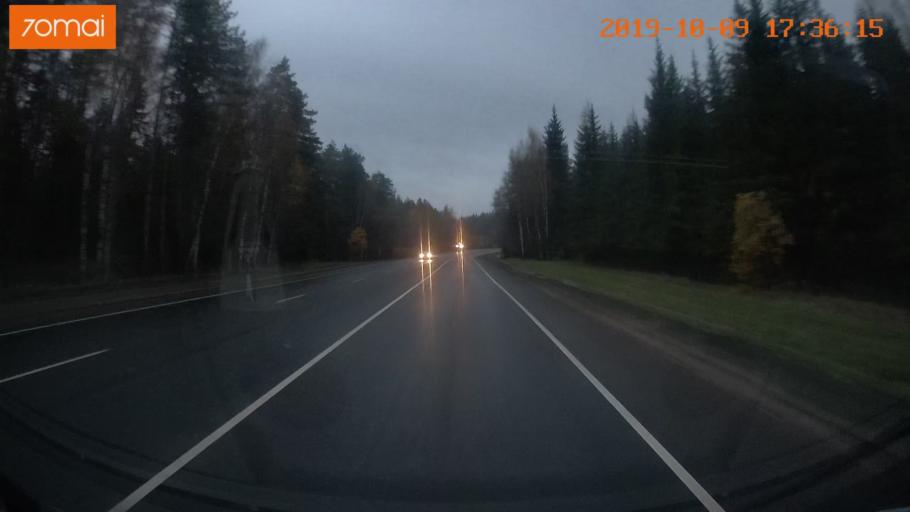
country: RU
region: Ivanovo
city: Bogorodskoye
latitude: 57.0810
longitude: 40.9980
